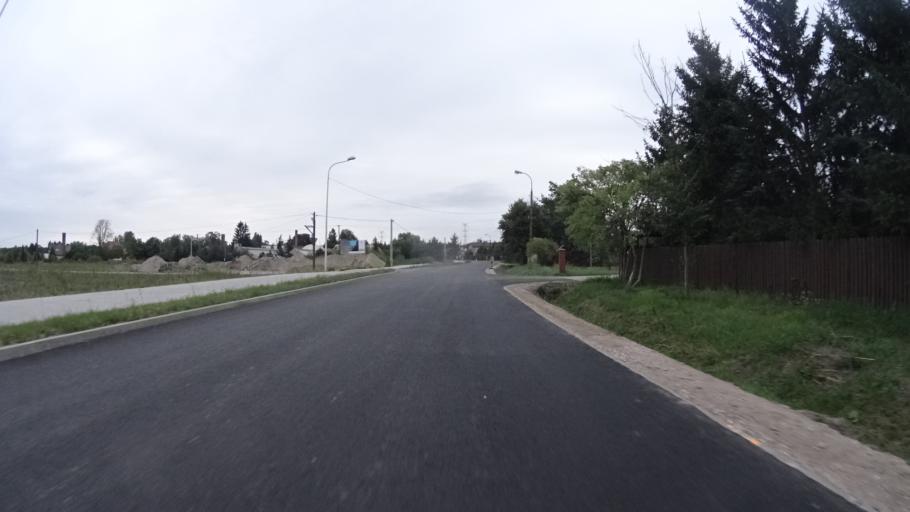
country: PL
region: Masovian Voivodeship
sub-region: Powiat warszawski zachodni
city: Stare Babice
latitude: 52.2666
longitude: 20.8278
